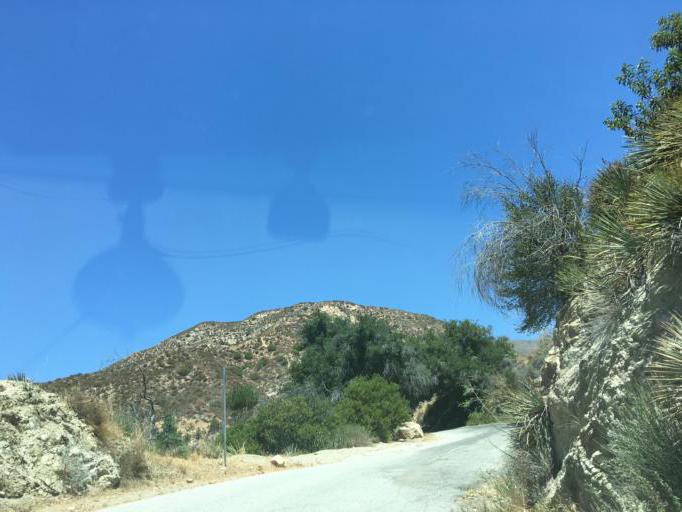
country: US
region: California
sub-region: Los Angeles County
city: La Crescenta-Montrose
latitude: 34.2879
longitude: -118.2259
